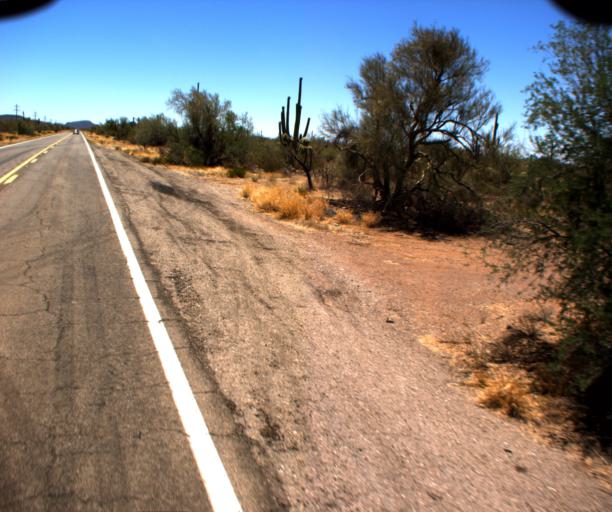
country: US
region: Arizona
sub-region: Pima County
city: Sells
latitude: 32.0235
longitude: -112.0041
